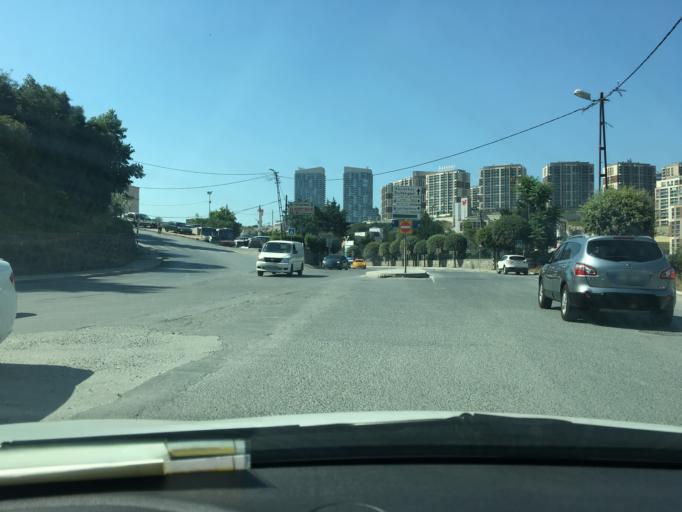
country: TR
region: Istanbul
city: Sisli
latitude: 41.0835
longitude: 28.9485
